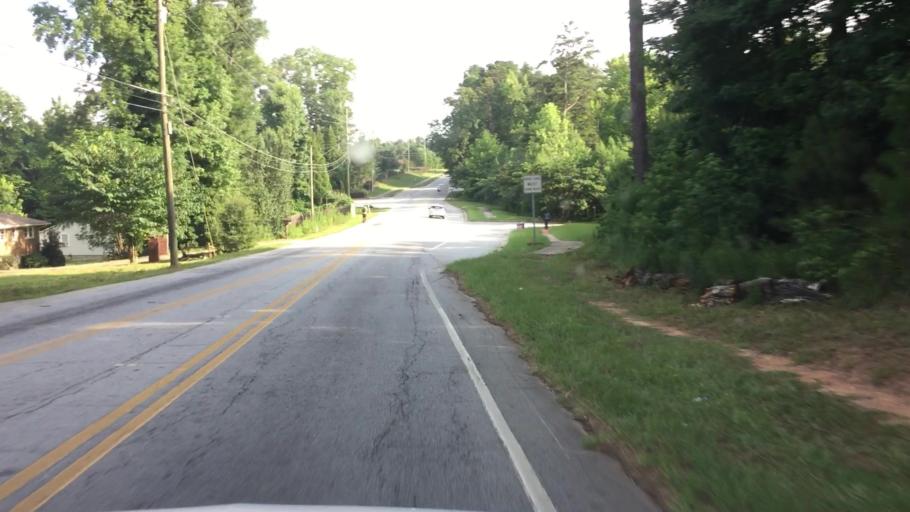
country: US
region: Georgia
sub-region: DeKalb County
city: Lithonia
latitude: 33.6979
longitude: -84.1084
